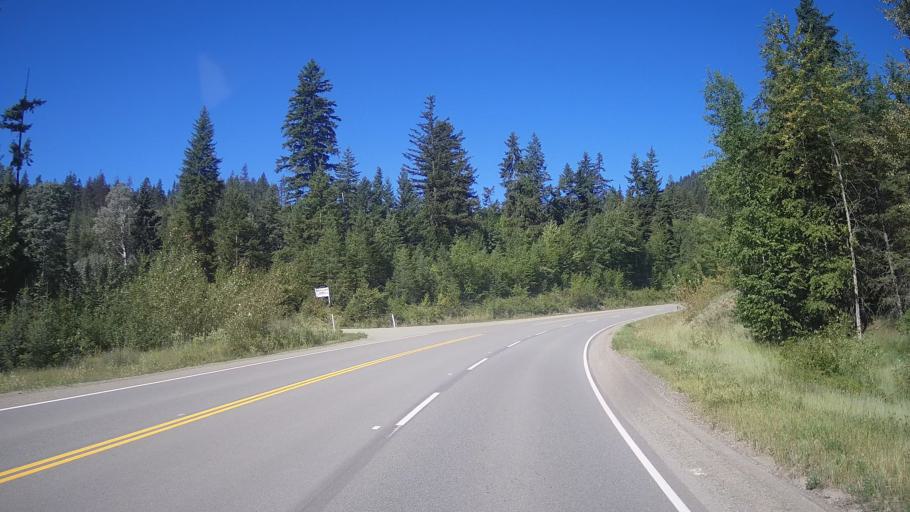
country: CA
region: British Columbia
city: Kamloops
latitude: 51.4621
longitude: -120.2439
